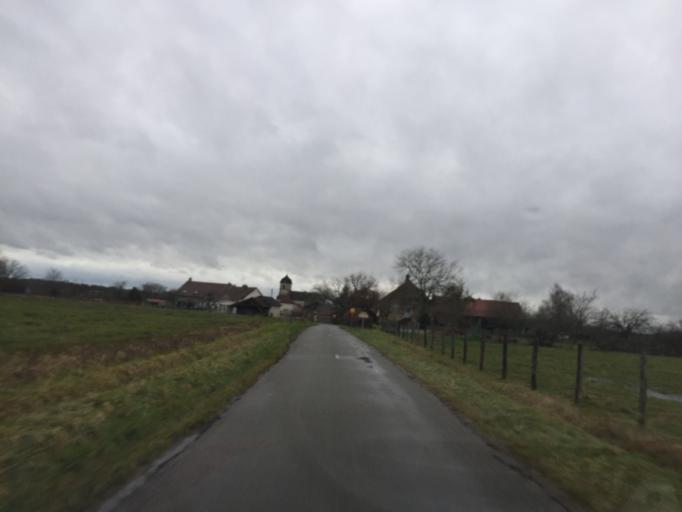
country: FR
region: Franche-Comte
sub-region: Departement du Jura
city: Champvans
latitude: 47.1443
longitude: 5.4361
